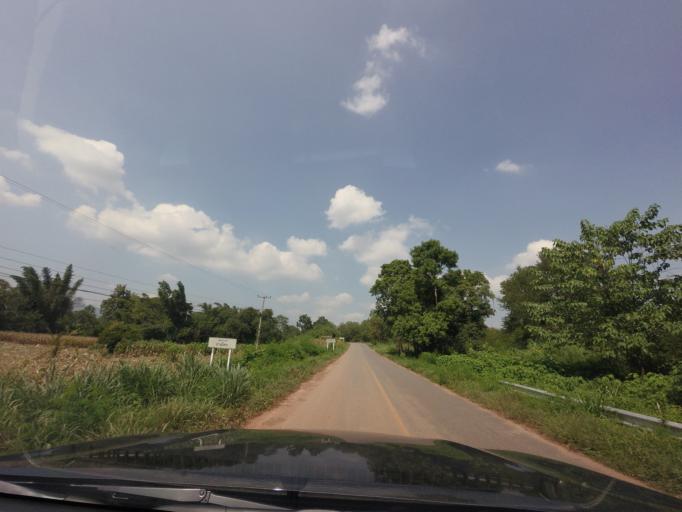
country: TH
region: Uttaradit
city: Fak Tha
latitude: 17.8965
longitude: 100.9776
